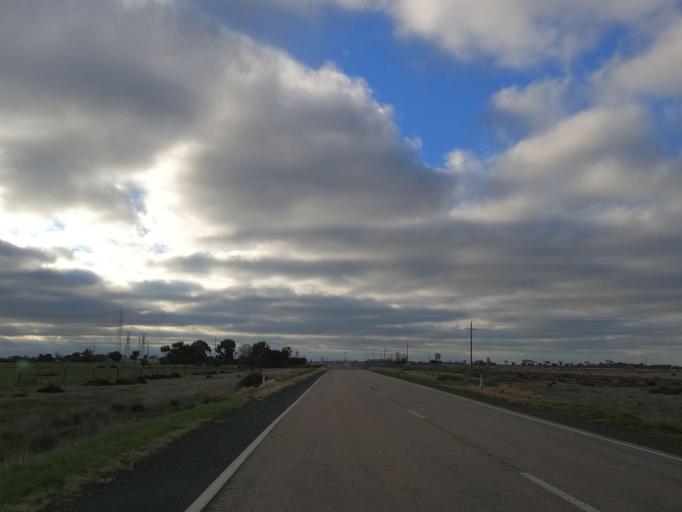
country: AU
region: Victoria
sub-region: Swan Hill
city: Swan Hill
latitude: -35.7783
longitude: 143.9357
